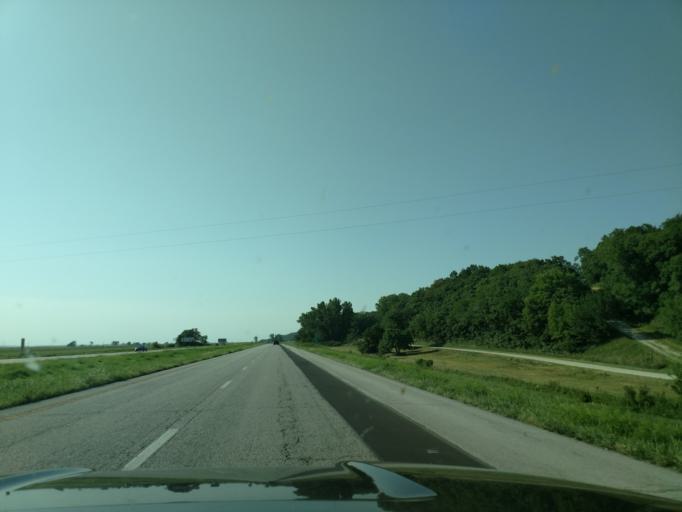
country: US
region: Missouri
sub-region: Atchison County
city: Rock Port
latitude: 40.4177
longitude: -95.5610
